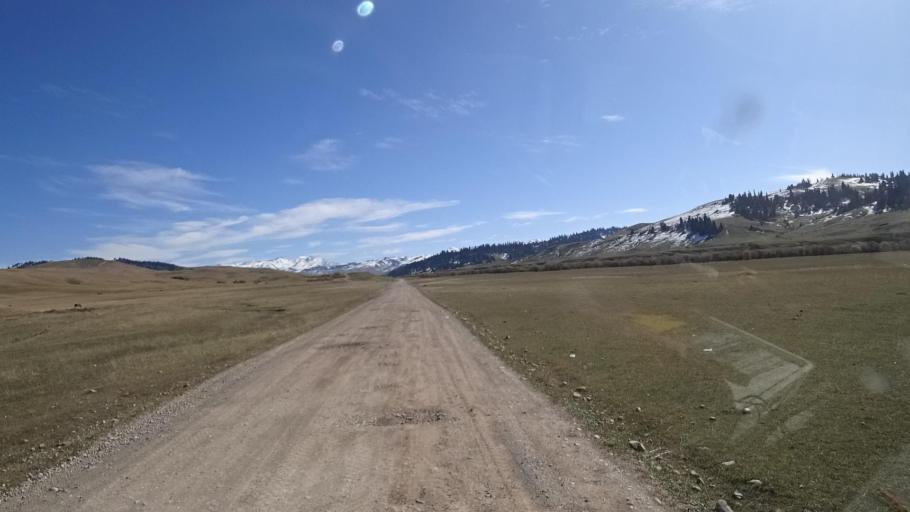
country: KZ
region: Almaty Oblysy
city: Kegen
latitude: 42.7412
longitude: 79.0030
